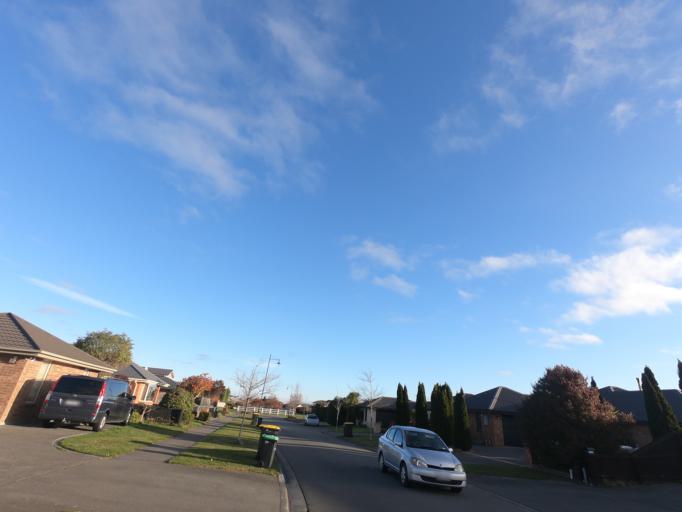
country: NZ
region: Canterbury
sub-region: Selwyn District
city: Prebbleton
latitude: -43.5662
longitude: 172.5674
